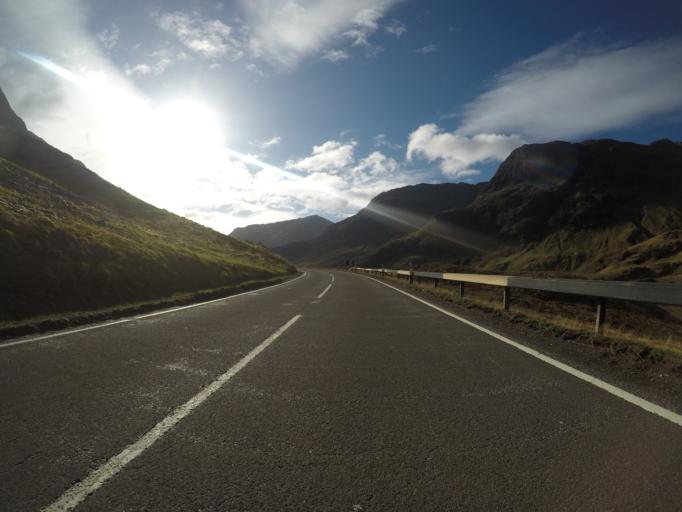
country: GB
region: Scotland
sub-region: Highland
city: Fort William
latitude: 56.6686
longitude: -4.9973
